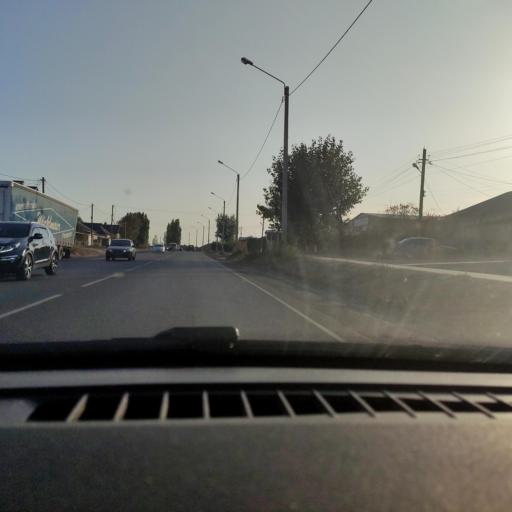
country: RU
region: Voronezj
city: Pridonskoy
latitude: 51.7113
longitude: 39.0741
